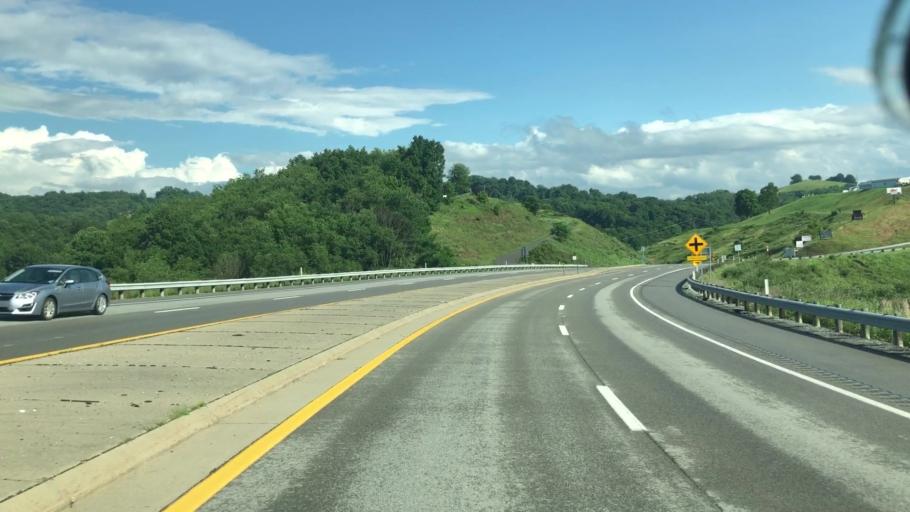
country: US
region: West Virginia
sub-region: Harrison County
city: Bridgeport
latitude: 39.3023
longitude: -80.2076
